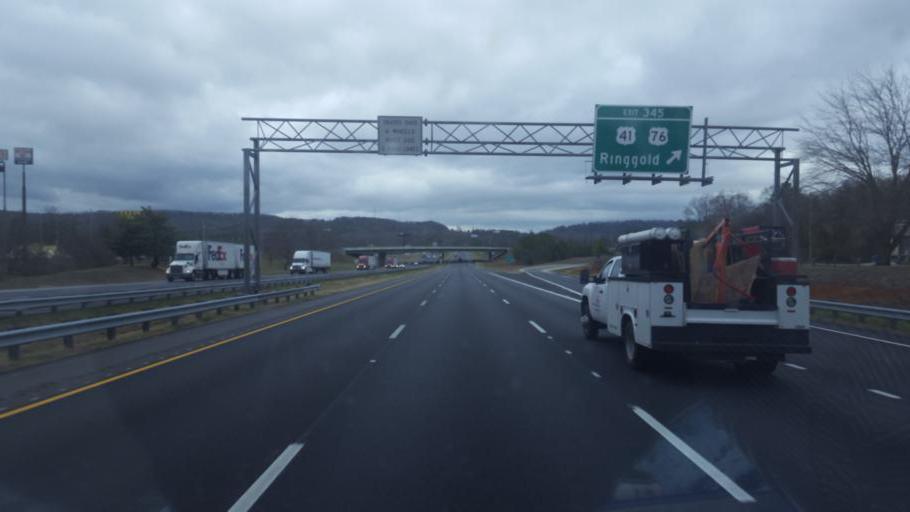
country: US
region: Georgia
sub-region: Catoosa County
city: Ringgold
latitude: 34.8905
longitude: -85.0703
